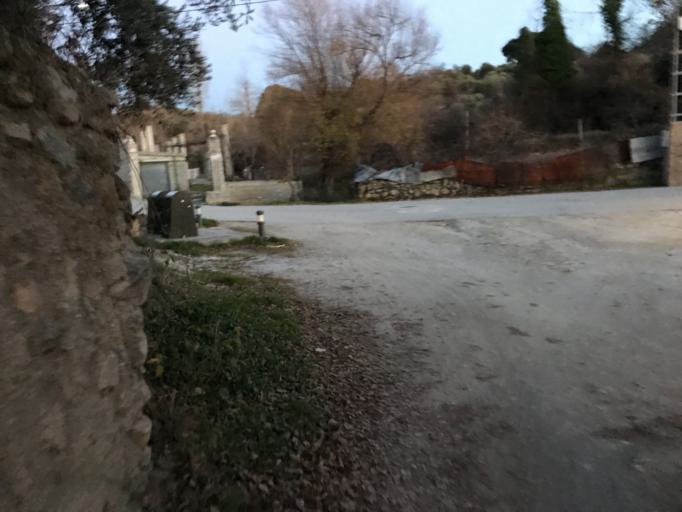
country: ES
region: Andalusia
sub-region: Provincia de Granada
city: Beas de Granada
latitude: 37.2208
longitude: -3.4779
